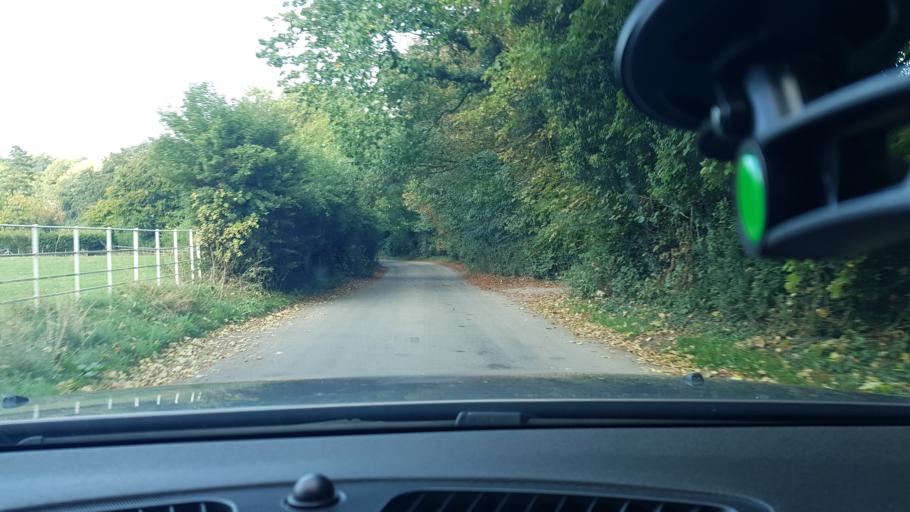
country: GB
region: England
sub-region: West Berkshire
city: Lambourn
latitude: 51.5141
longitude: -1.5384
